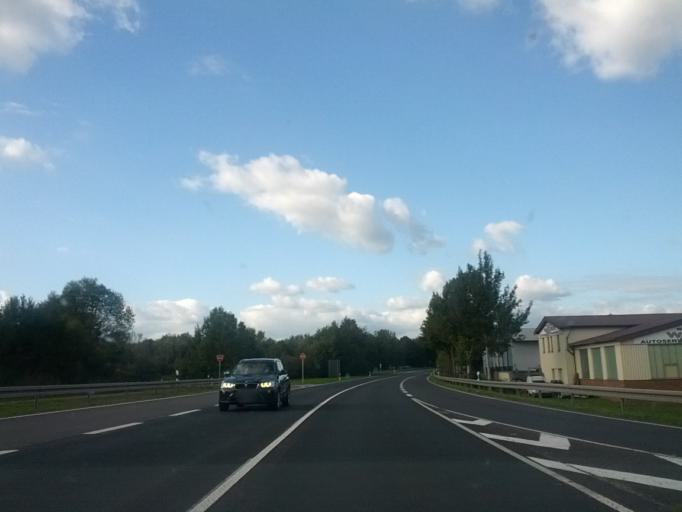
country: DE
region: Thuringia
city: Fambach
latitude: 50.7413
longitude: 10.3573
